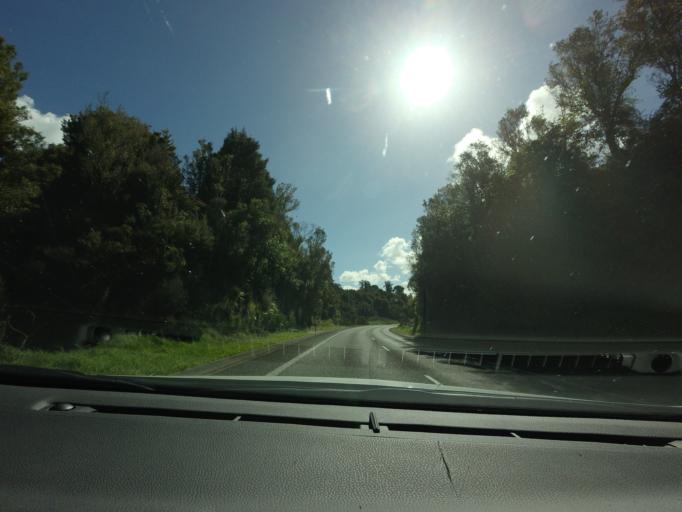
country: NZ
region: Waikato
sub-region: South Waikato District
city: Tokoroa
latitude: -38.0316
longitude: 175.9899
